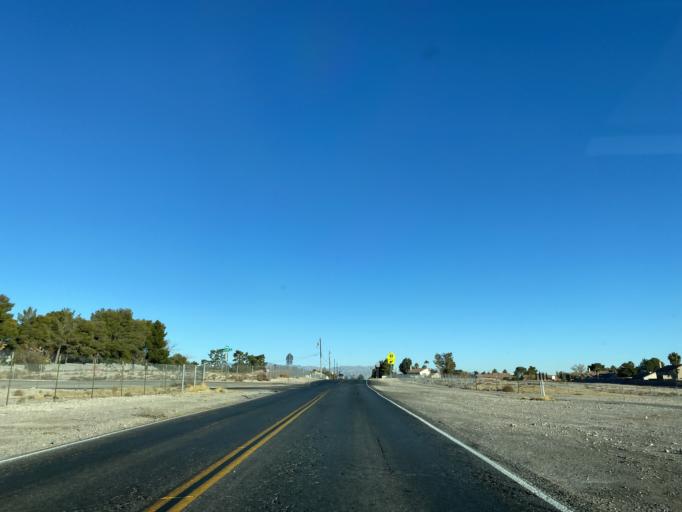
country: US
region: Nevada
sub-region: Clark County
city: Whitney
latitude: 36.0821
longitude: -115.1099
